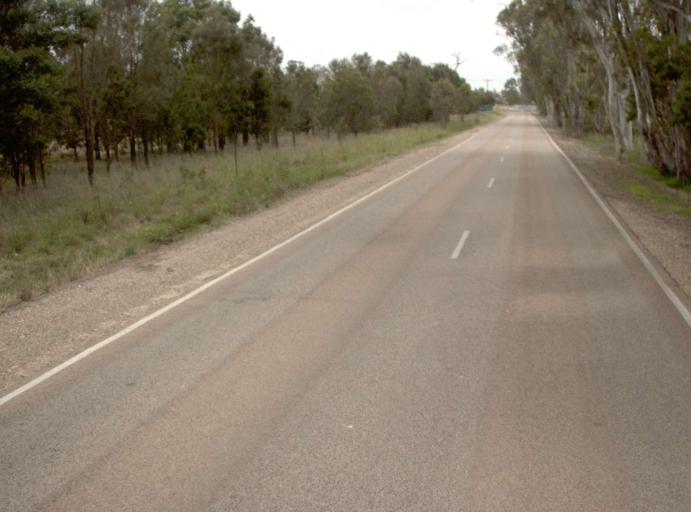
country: AU
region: Victoria
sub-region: East Gippsland
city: Bairnsdale
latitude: -37.8779
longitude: 147.4233
